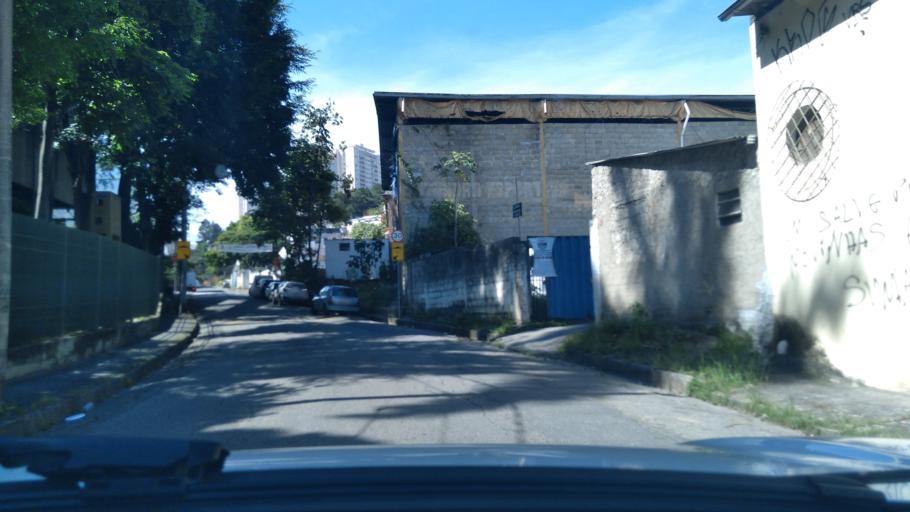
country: BR
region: Minas Gerais
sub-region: Belo Horizonte
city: Belo Horizonte
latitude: -19.8951
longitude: -43.9663
